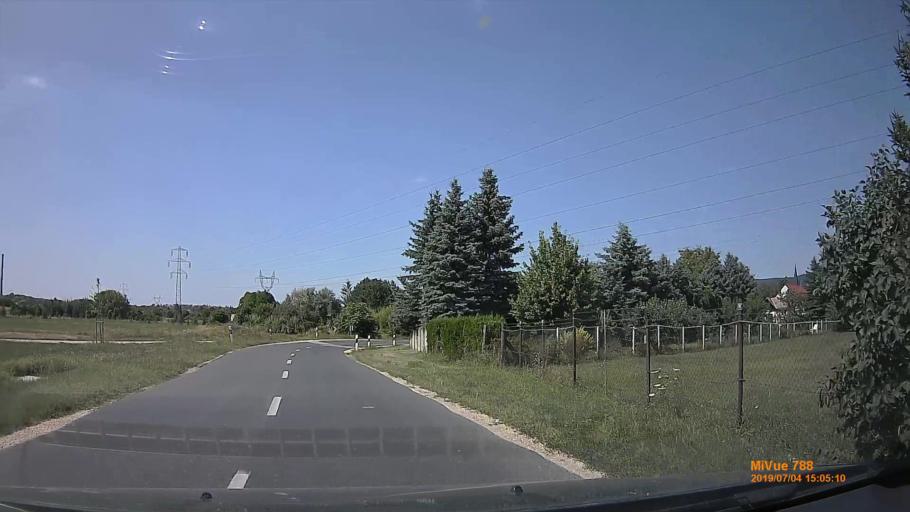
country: HU
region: Komarom-Esztergom
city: Tatabanya
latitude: 47.5660
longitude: 18.3893
